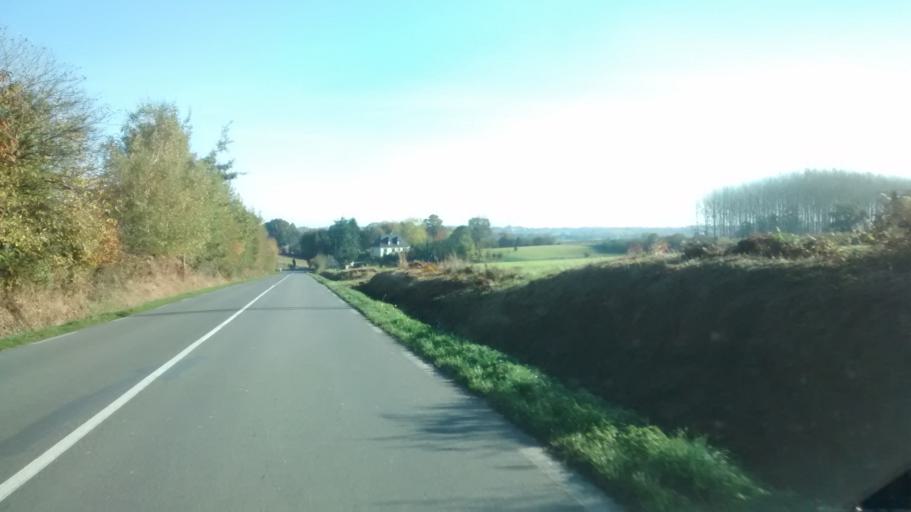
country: FR
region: Brittany
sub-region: Departement d'Ille-et-Vilaine
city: Poce-les-Bois
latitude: 48.0867
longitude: -1.2453
